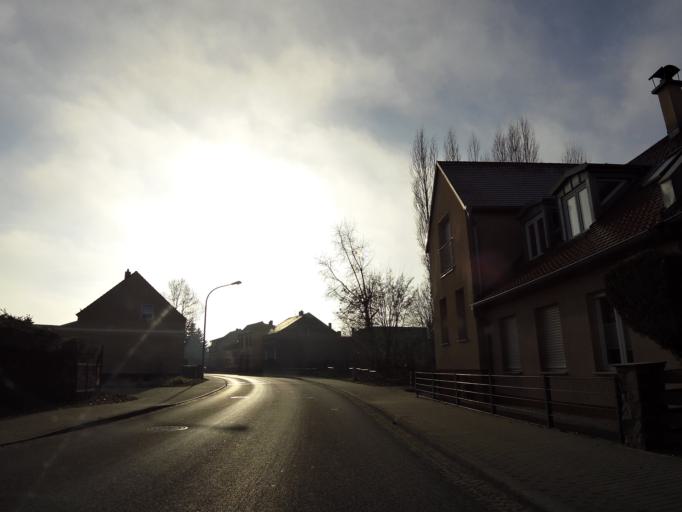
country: DE
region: Brandenburg
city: Werder
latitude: 52.3629
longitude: 12.9091
